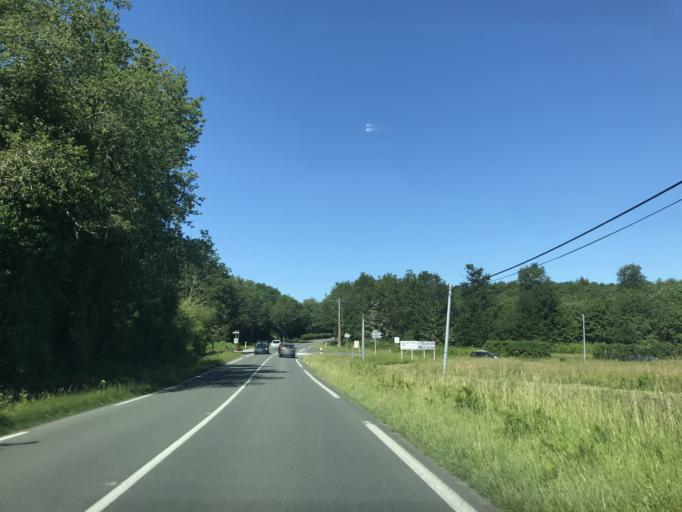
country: FR
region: Poitou-Charentes
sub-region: Departement de la Charente-Maritime
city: Gemozac
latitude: 45.5701
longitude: -0.7504
